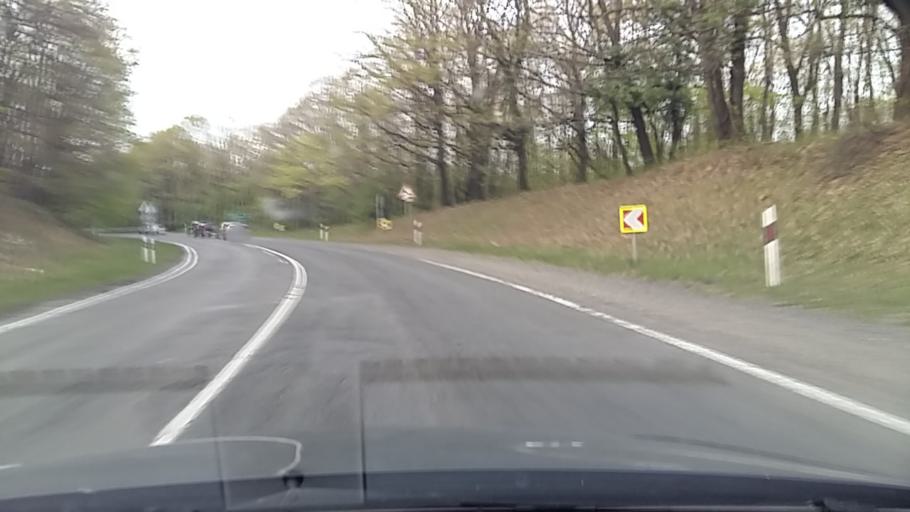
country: HU
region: Baranya
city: Mecseknadasd
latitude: 46.1916
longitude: 18.4526
